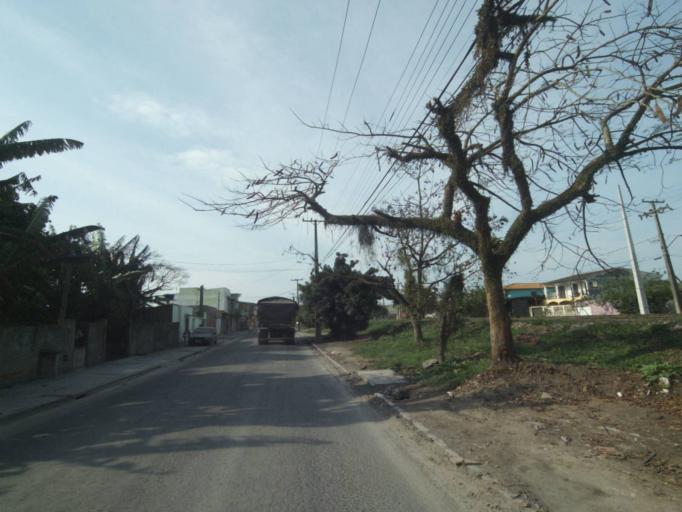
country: BR
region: Parana
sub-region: Paranagua
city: Paranagua
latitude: -25.5267
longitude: -48.5298
